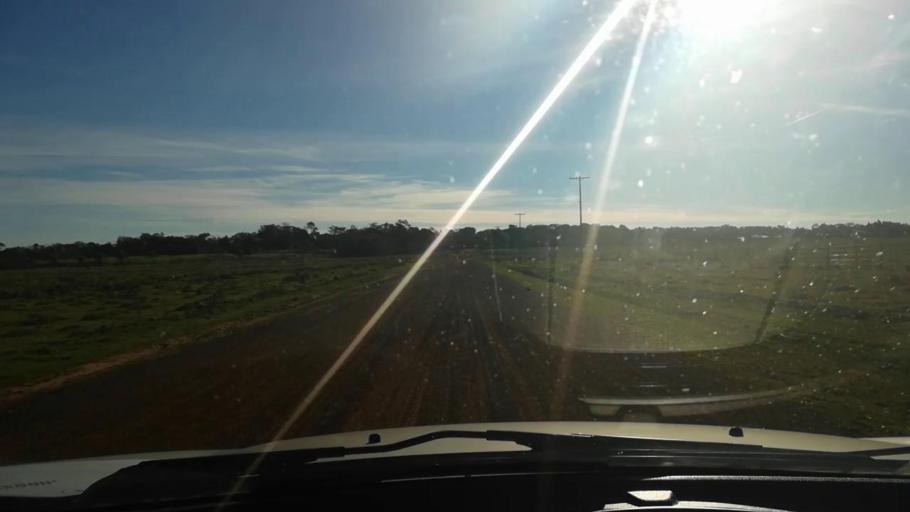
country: PY
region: Caaguazu
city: Coronel Oviedo
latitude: -25.5177
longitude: -56.4130
